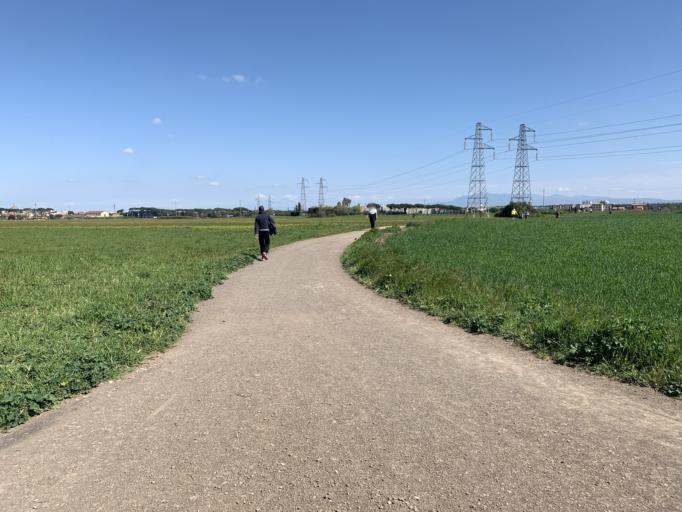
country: IT
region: Latium
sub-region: Citta metropolitana di Roma Capitale
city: Ciampino
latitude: 41.8374
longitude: 12.5702
